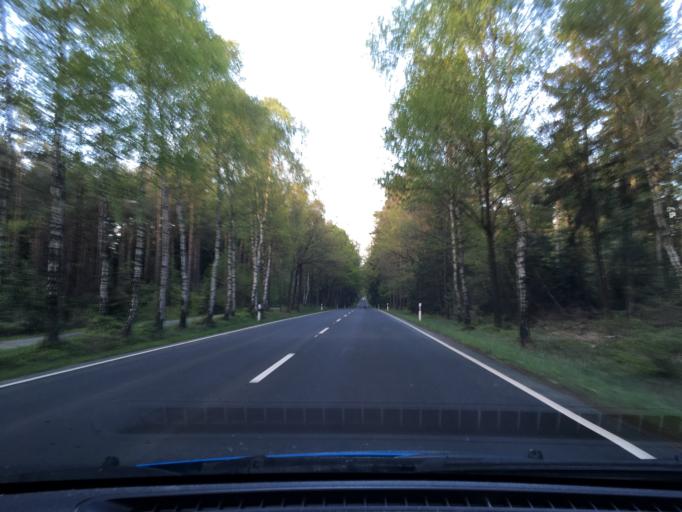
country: DE
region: Lower Saxony
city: Bispingen
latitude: 53.0494
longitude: 10.0111
